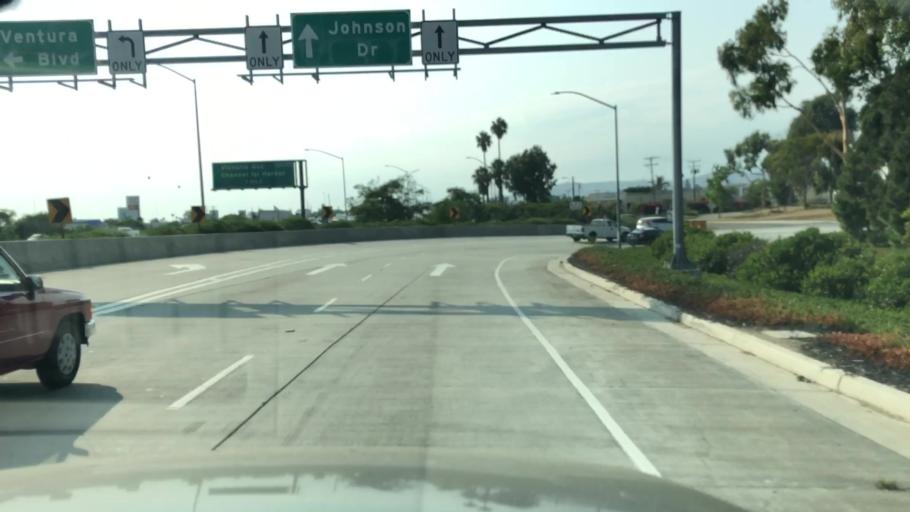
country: US
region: California
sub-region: Ventura County
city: El Rio
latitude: 34.2450
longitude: -119.1954
